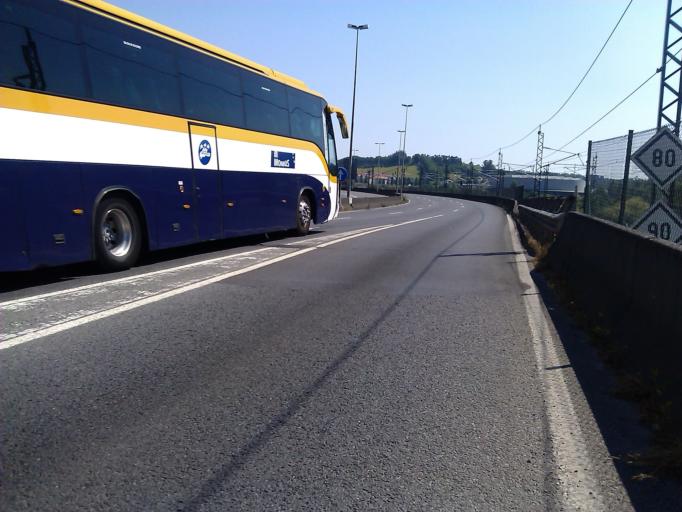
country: ES
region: Galicia
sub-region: Provincia da Coruna
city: Santiago de Compostela
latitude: 42.8734
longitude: -8.5379
